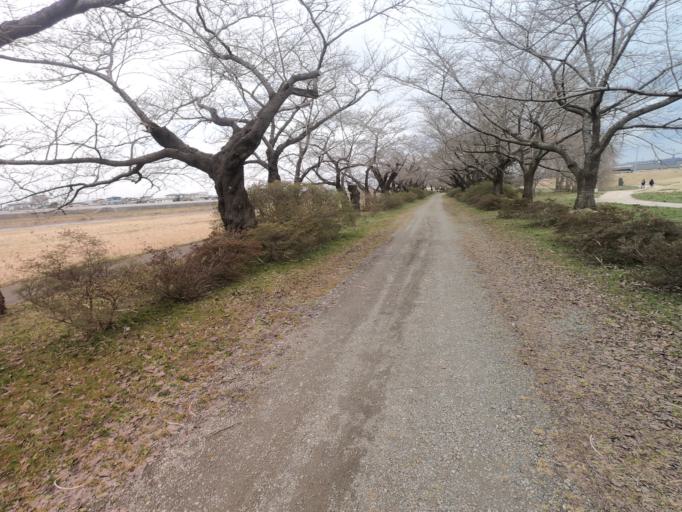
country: JP
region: Iwate
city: Kitakami
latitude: 39.2797
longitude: 141.1280
